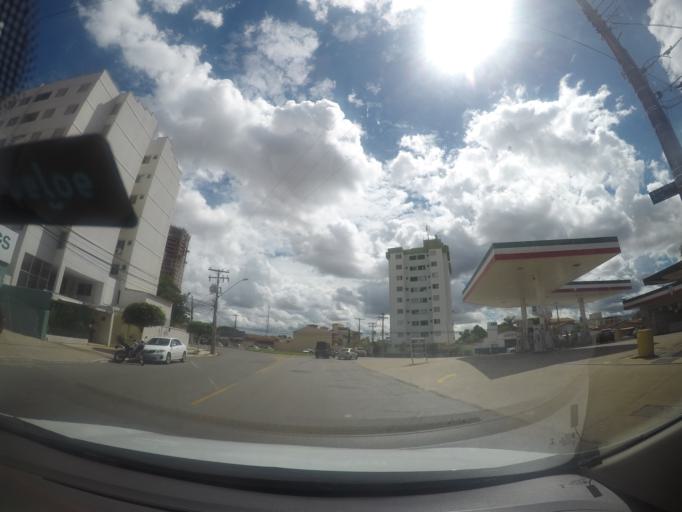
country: BR
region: Goias
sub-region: Goiania
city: Goiania
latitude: -16.6831
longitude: -49.2768
